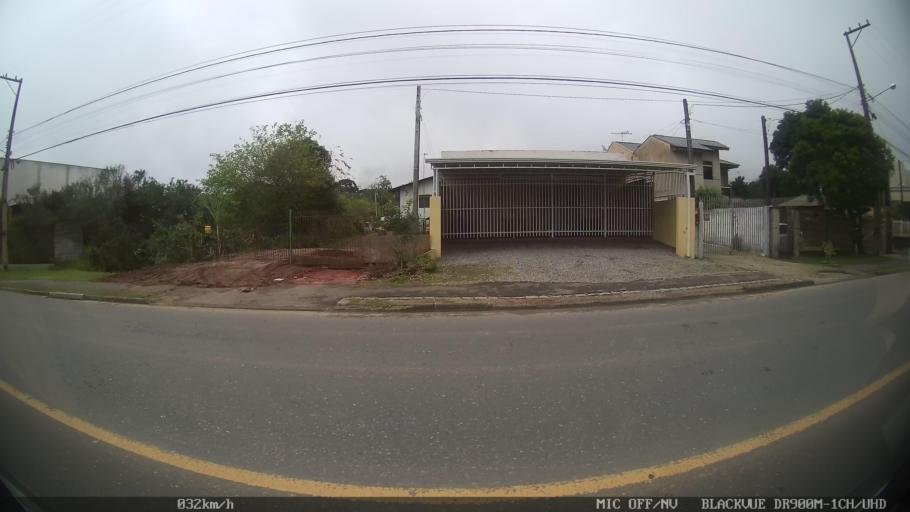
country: BR
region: Parana
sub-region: Sao Jose Dos Pinhais
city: Sao Jose dos Pinhais
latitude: -25.5726
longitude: -49.1716
